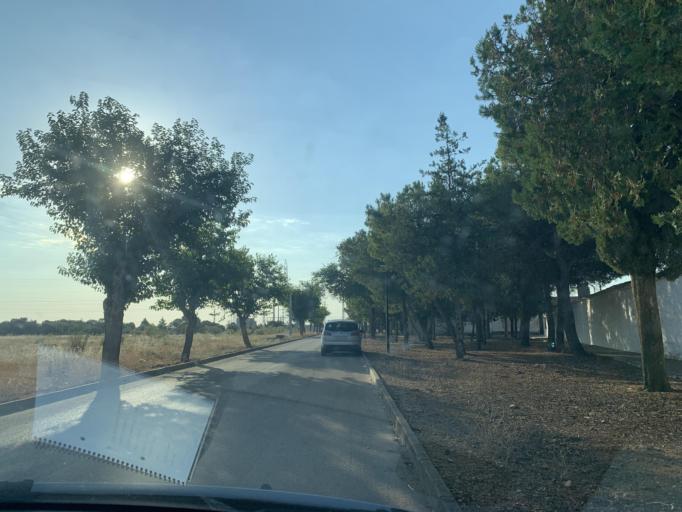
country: ES
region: Castille-La Mancha
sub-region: Provincia de Ciudad Real
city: Argamasilla de Alba
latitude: 39.1769
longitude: -3.2349
